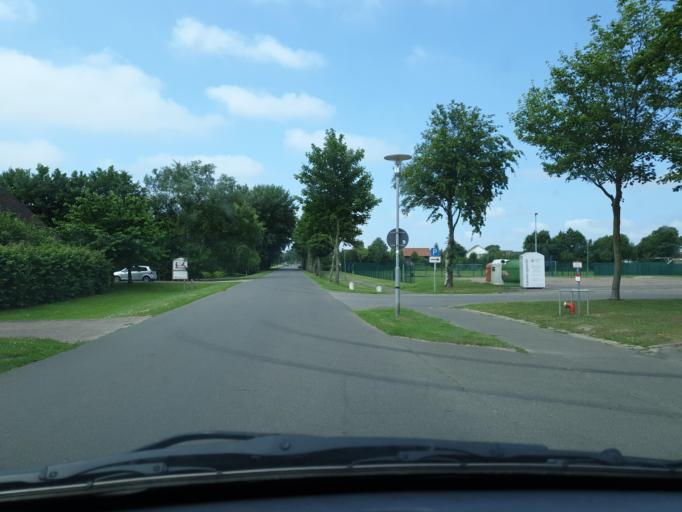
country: DE
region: Schleswig-Holstein
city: Friedrichskoog
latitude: 54.0032
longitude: 8.8768
